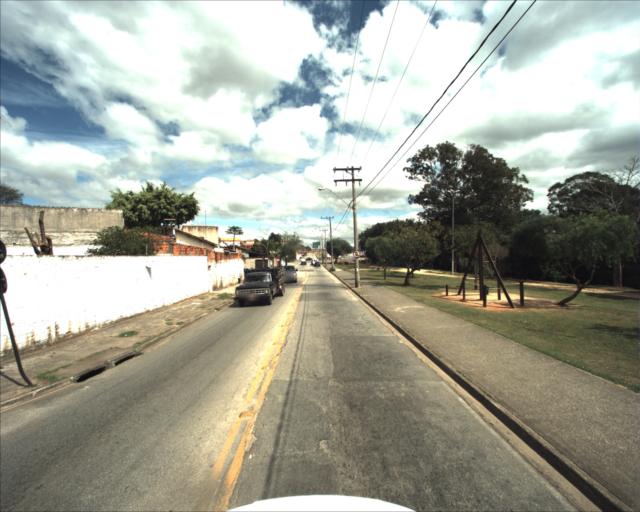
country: BR
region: Sao Paulo
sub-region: Sorocaba
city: Sorocaba
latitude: -23.5020
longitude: -47.5211
